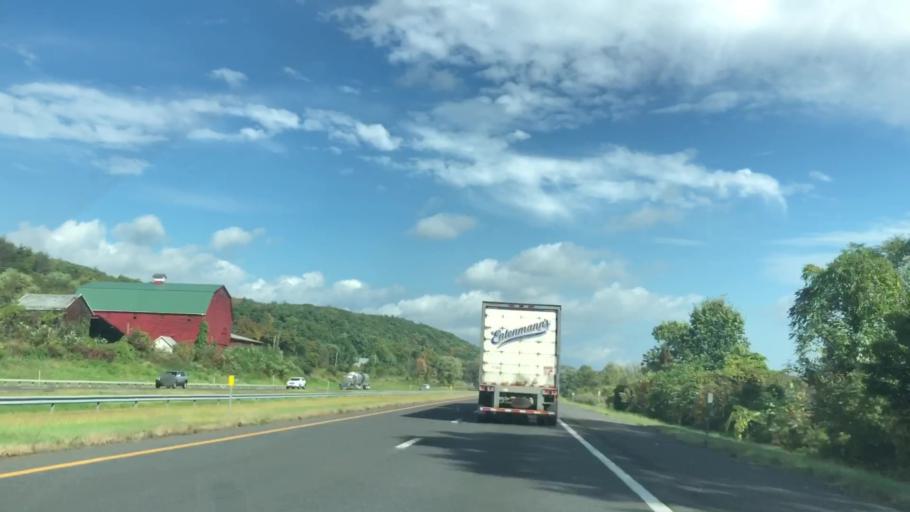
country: US
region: New York
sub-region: Ulster County
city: Lincoln Park
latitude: 41.9602
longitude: -74.0153
